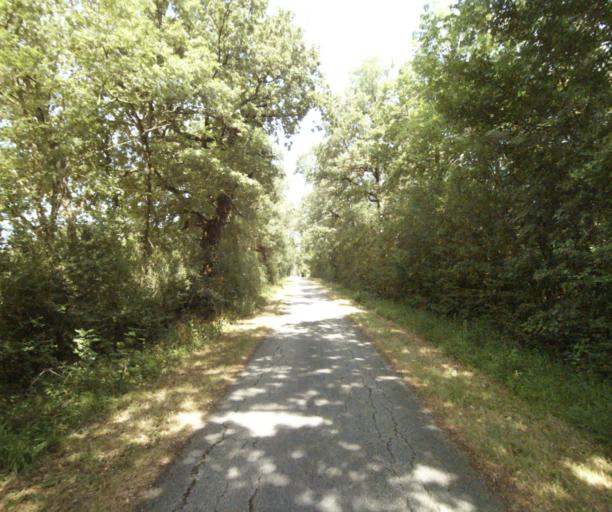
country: FR
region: Midi-Pyrenees
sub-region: Departement du Tarn
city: Dourgne
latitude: 43.4850
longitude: 2.1107
